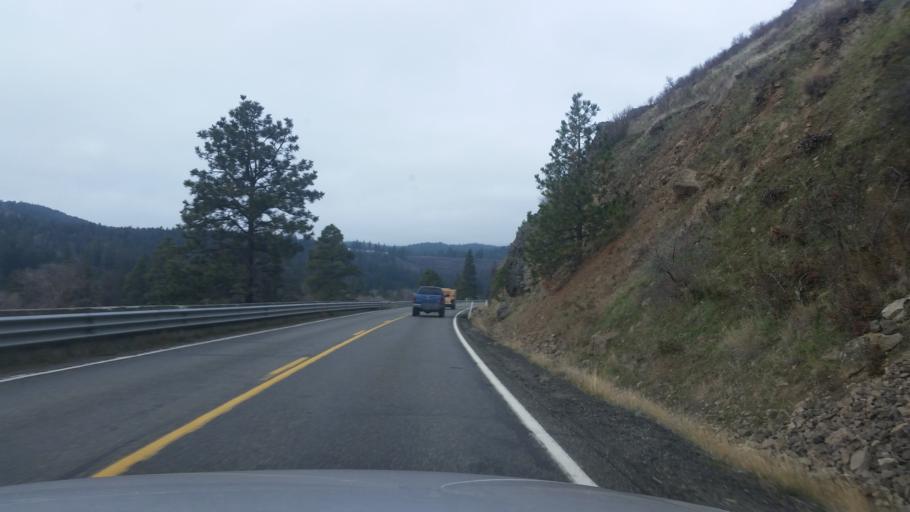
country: US
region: Washington
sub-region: Kittitas County
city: Cle Elum
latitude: 47.1315
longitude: -120.7801
